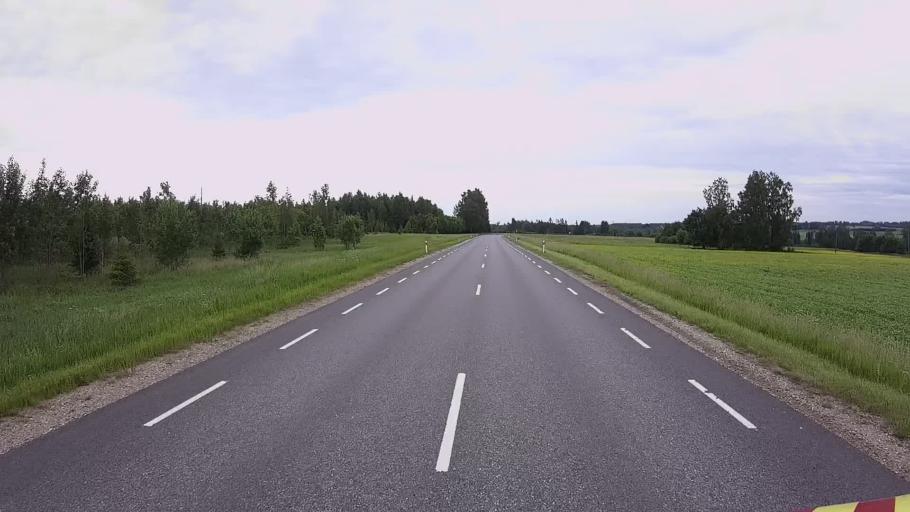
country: EE
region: Viljandimaa
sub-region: Karksi vald
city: Karksi-Nuia
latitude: 58.1561
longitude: 25.5949
